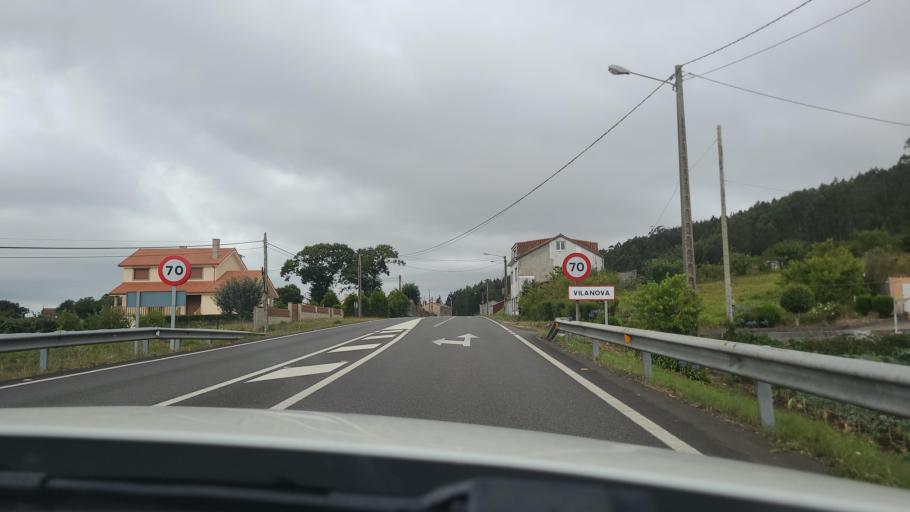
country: ES
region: Galicia
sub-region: Provincia da Coruna
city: Cee
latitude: 42.9936
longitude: -9.1818
